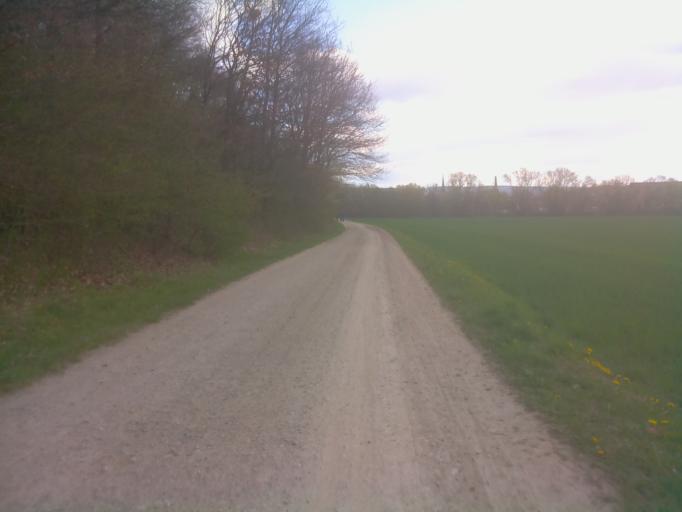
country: DE
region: Thuringia
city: Kahla
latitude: 50.8151
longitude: 11.5890
